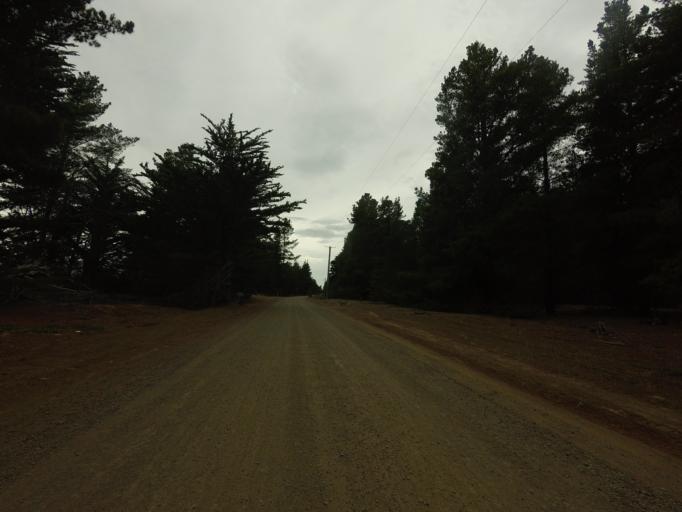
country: AU
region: Tasmania
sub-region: Clarence
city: Seven Mile Beach
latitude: -42.8345
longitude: 147.5350
